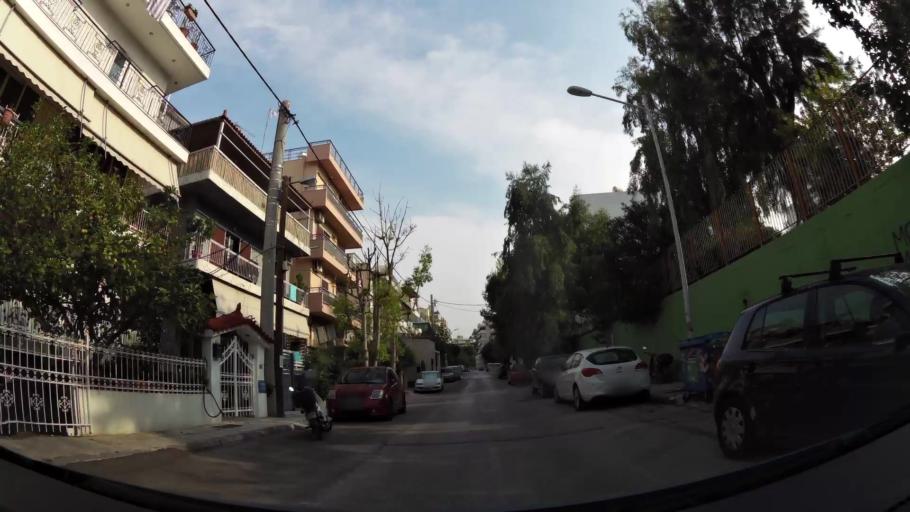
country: GR
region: Attica
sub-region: Nomarchia Athinas
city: Agios Dimitrios
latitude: 37.9283
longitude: 23.7219
